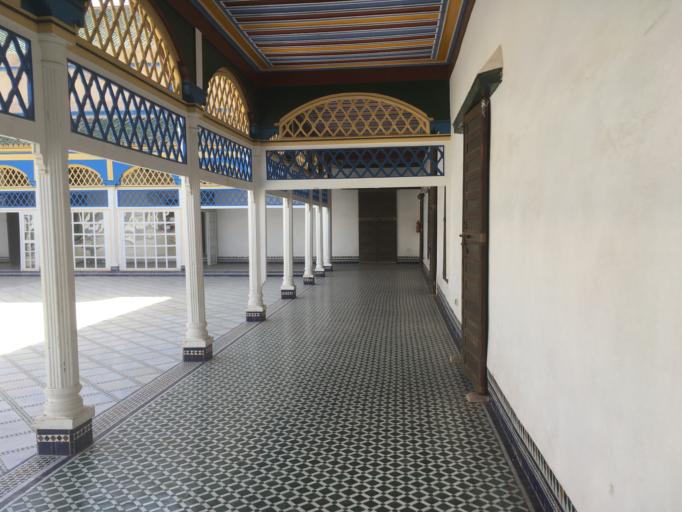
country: MA
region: Marrakech-Tensift-Al Haouz
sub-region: Marrakech
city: Marrakesh
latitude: 31.6217
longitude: -7.9815
